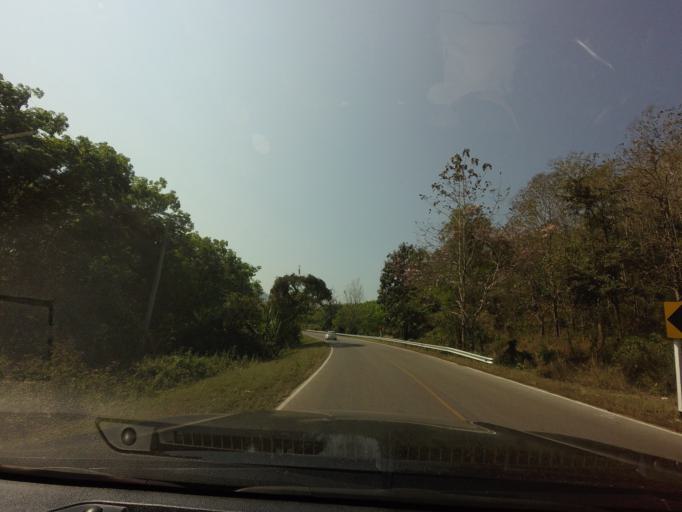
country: TH
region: Kanchanaburi
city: Thong Pha Phum
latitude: 14.6716
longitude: 98.5285
